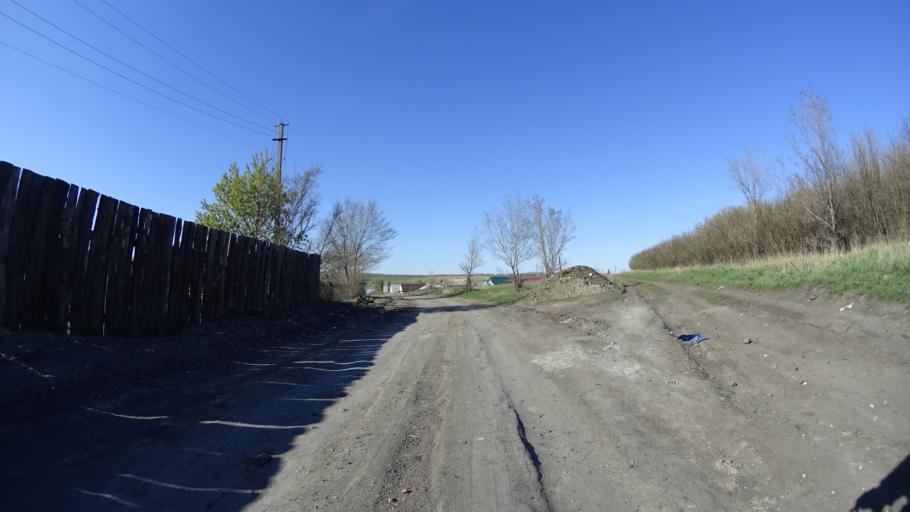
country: RU
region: Chelyabinsk
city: Troitsk
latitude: 54.0892
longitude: 61.5999
